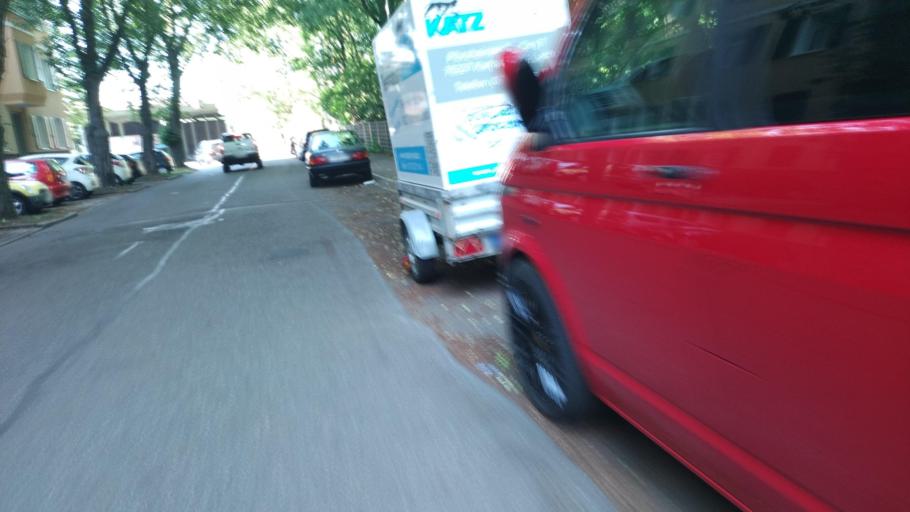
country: DE
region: Baden-Wuerttemberg
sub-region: Karlsruhe Region
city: Karlsruhe
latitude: 49.0002
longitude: 8.4603
